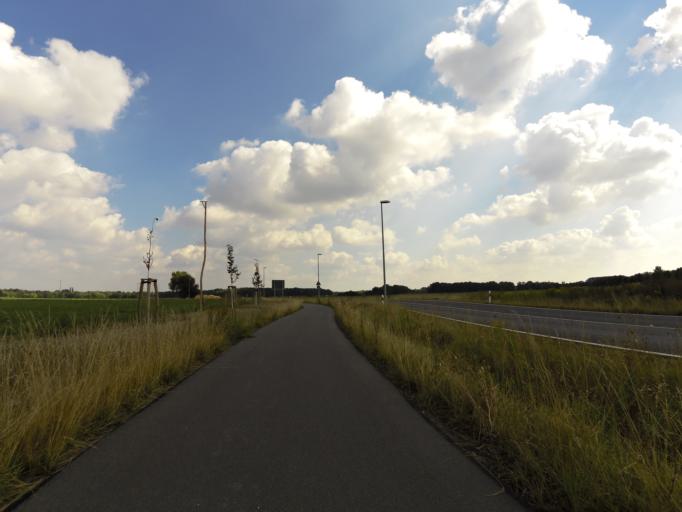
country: DE
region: Berlin
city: Lichtenrade
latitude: 52.3684
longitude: 13.3969
